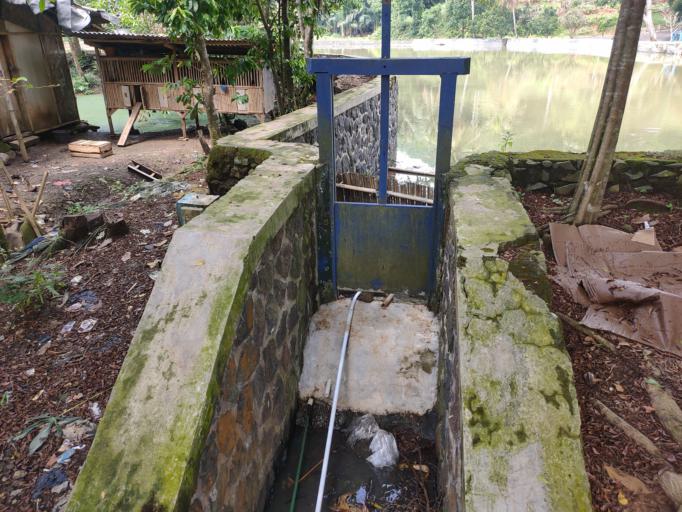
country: ID
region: West Java
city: Ciampea
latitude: -6.5195
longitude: 106.6863
